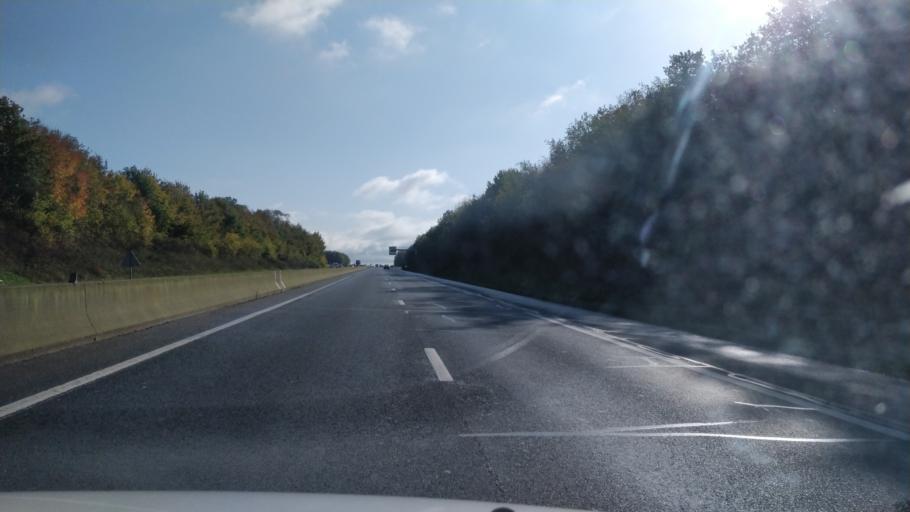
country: FR
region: Lower Normandy
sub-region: Departement du Calvados
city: Bretteville-sur-Odon
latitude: 49.1567
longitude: -0.4240
